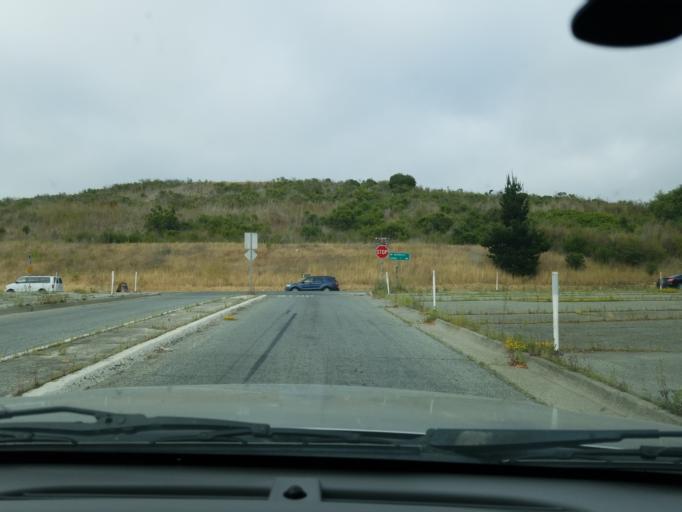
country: US
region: California
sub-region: Monterey County
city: Las Lomas
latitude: 36.8684
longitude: -121.7441
